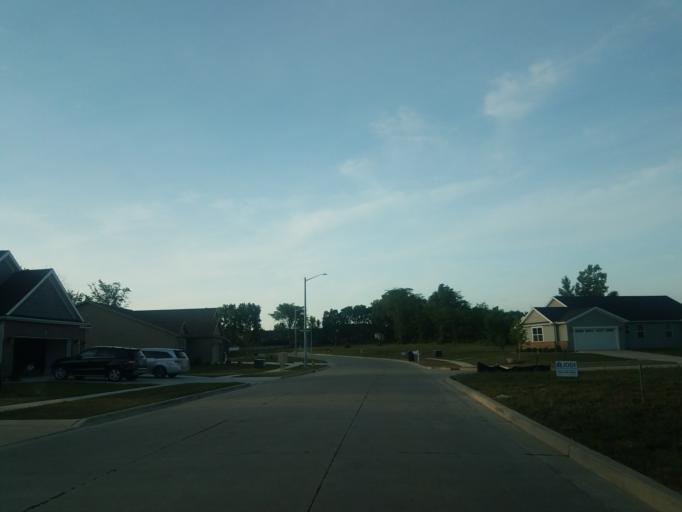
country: US
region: Illinois
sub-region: McLean County
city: Bloomington
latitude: 40.4452
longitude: -89.0084
